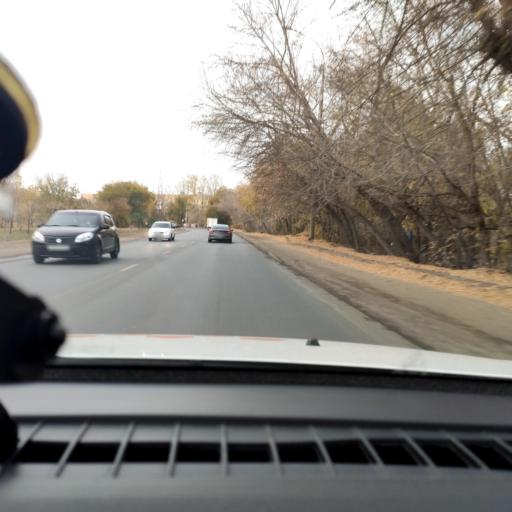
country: RU
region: Samara
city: Rozhdestveno
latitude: 53.1463
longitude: 50.0534
